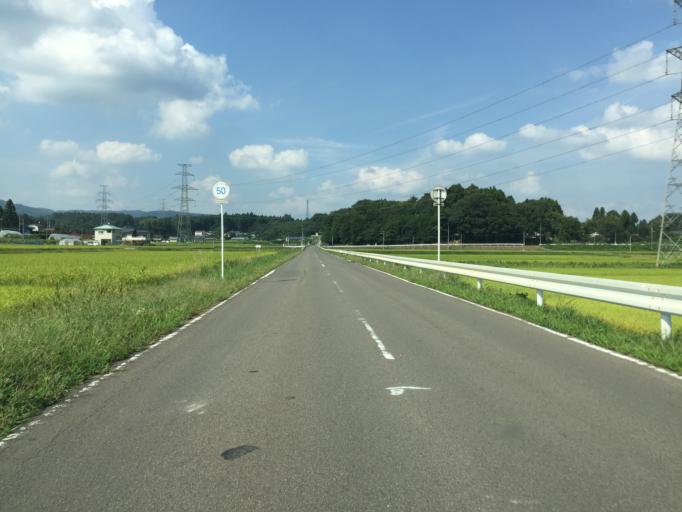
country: JP
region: Fukushima
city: Nihommatsu
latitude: 37.5642
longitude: 140.3841
